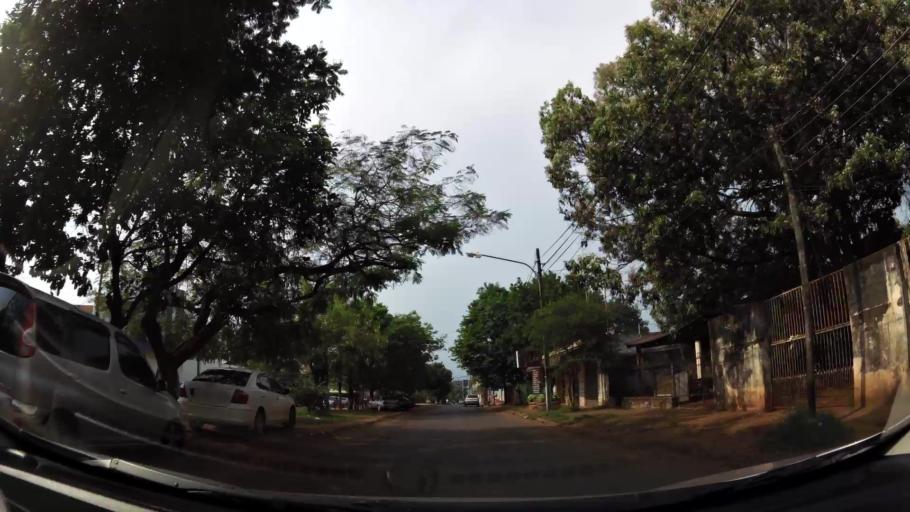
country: PY
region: Alto Parana
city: Ciudad del Este
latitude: -25.4988
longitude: -54.6512
